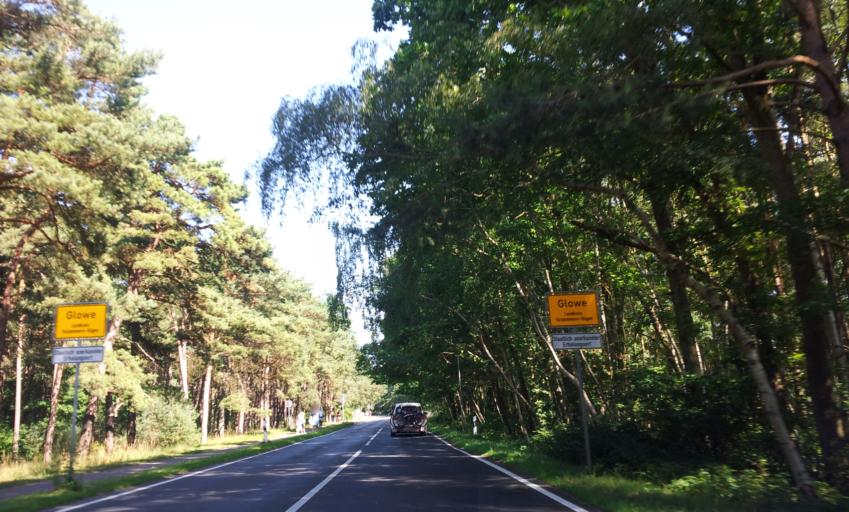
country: DE
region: Mecklenburg-Vorpommern
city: Glowe
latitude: 54.5695
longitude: 13.4517
